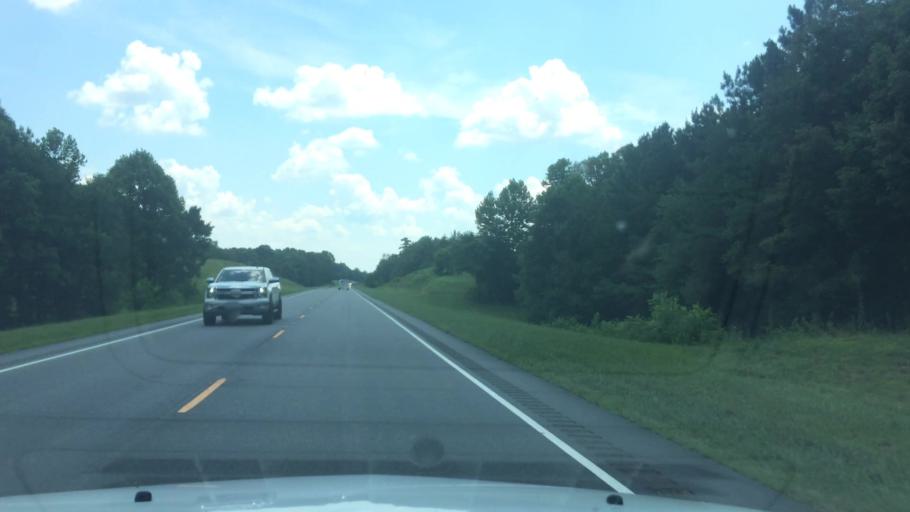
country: US
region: North Carolina
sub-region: Alexander County
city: Stony Point
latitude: 35.8782
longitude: -81.0707
